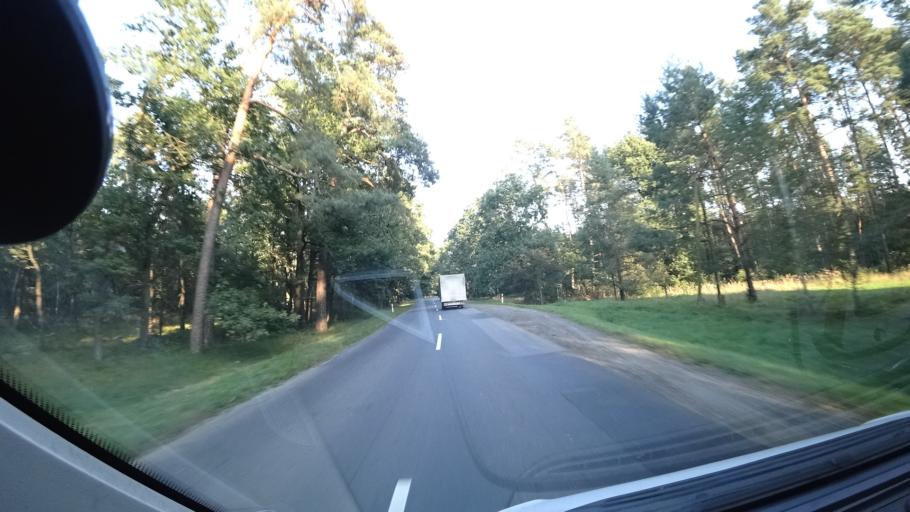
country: PL
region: Opole Voivodeship
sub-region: Powiat kedzierzynsko-kozielski
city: Dziergowice
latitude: 50.2798
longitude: 18.3567
